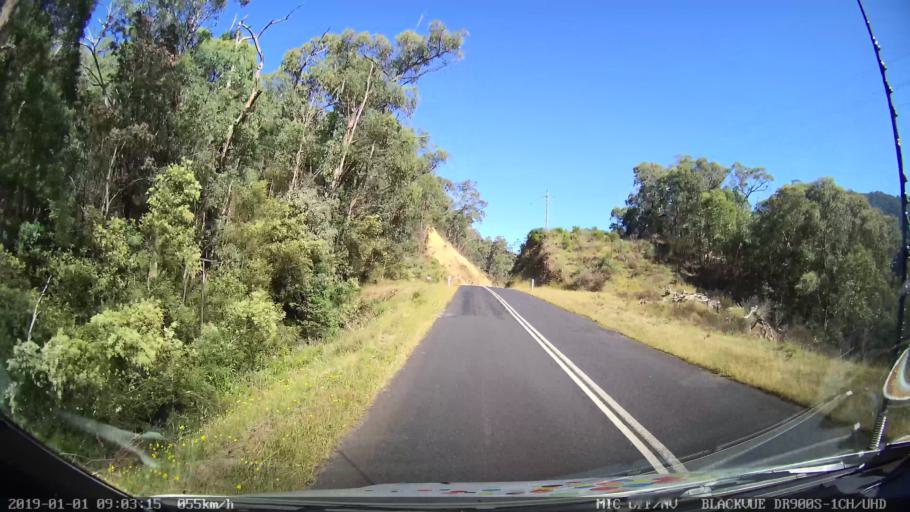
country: AU
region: New South Wales
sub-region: Snowy River
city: Jindabyne
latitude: -36.2247
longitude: 148.1659
